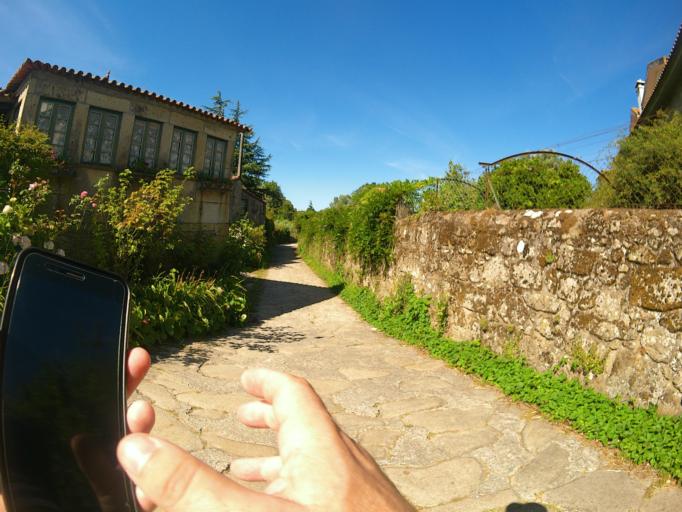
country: PT
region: Viana do Castelo
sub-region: Viana do Castelo
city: Darque
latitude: 41.7235
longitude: -8.6762
